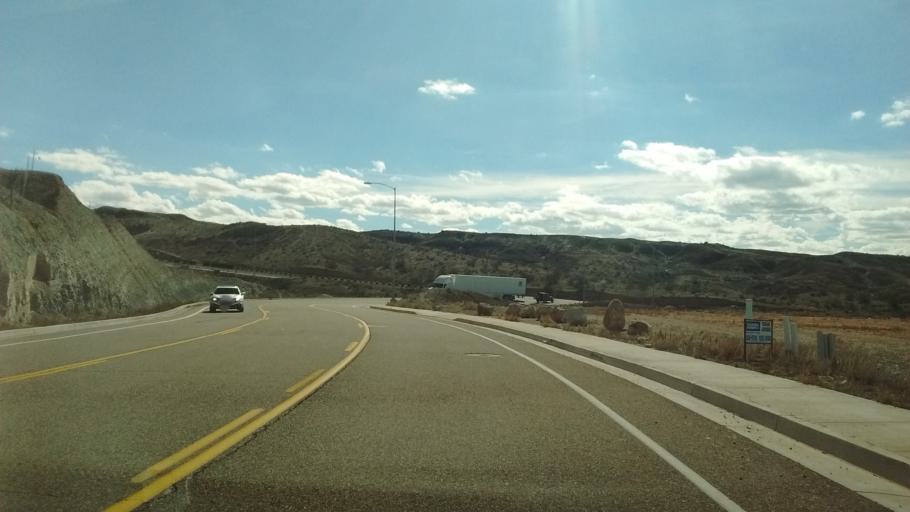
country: US
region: Utah
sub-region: Washington County
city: Saint George
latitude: 37.0600
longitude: -113.5810
